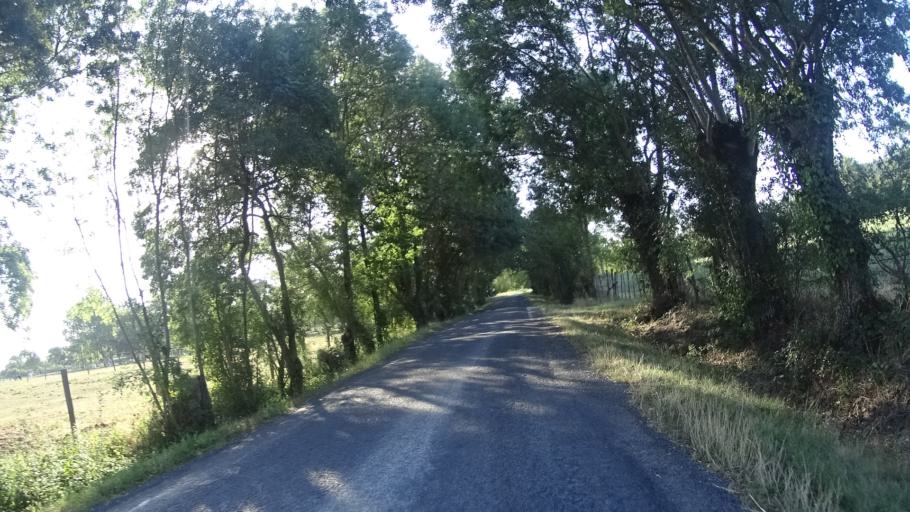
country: FR
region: Pays de la Loire
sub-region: Departement de Maine-et-Loire
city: Villebernier
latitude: 47.2738
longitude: -0.0075
